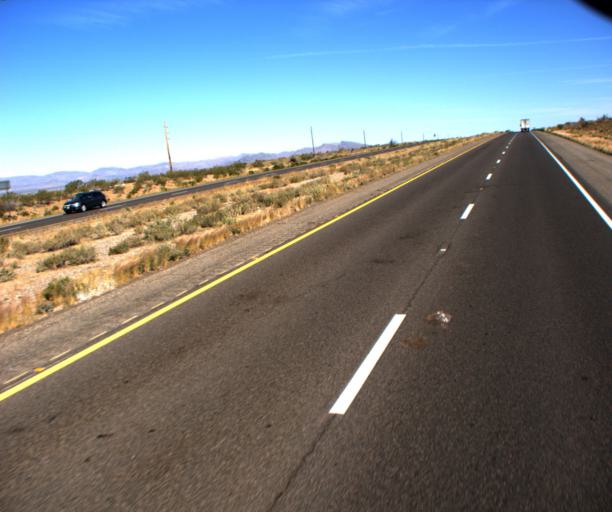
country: US
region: Arizona
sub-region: Mohave County
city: Golden Valley
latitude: 35.2450
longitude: -114.1491
